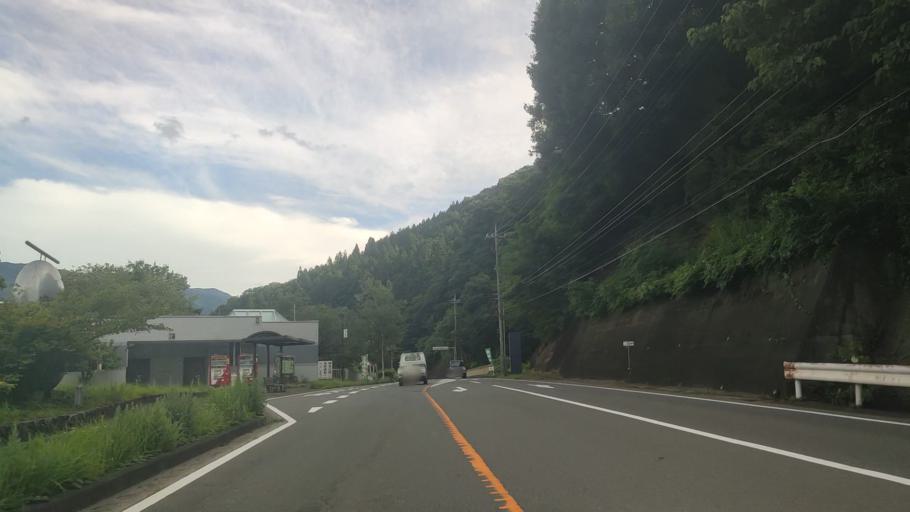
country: JP
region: Gunma
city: Omamacho-omama
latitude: 36.5528
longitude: 139.3724
